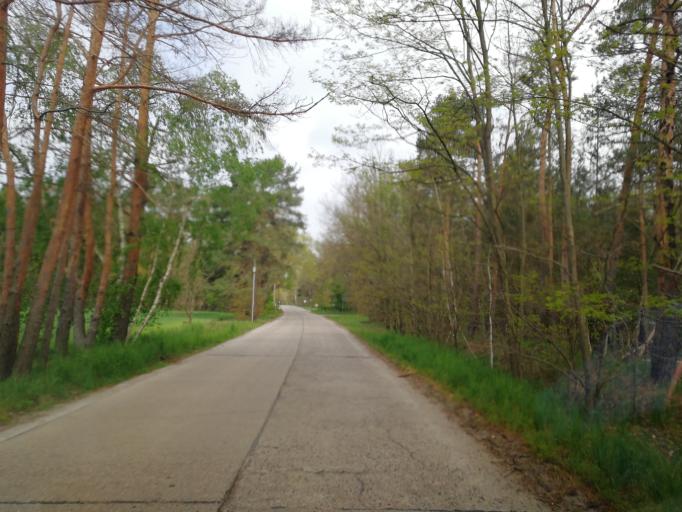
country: DE
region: Saxony
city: Beilrode
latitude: 51.6541
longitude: 13.1146
